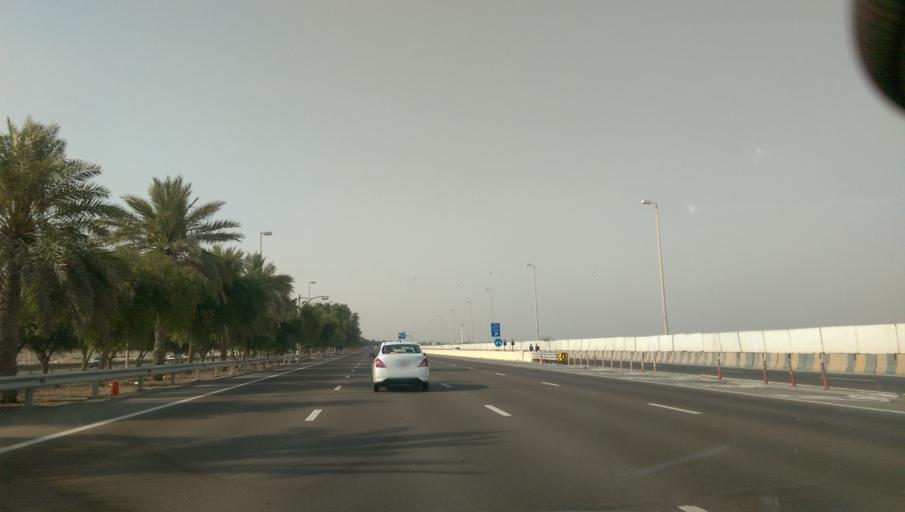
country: AE
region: Abu Dhabi
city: Abu Dhabi
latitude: 24.4282
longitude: 54.6776
